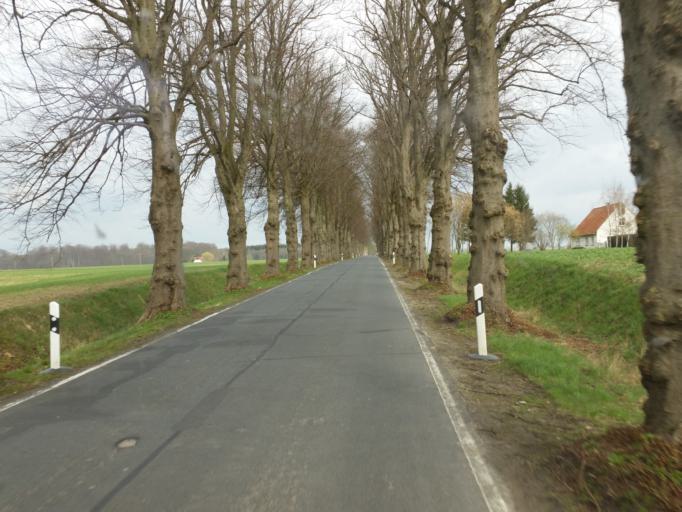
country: DE
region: Mecklenburg-Vorpommern
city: Wittenhagen
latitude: 54.2196
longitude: 13.0651
